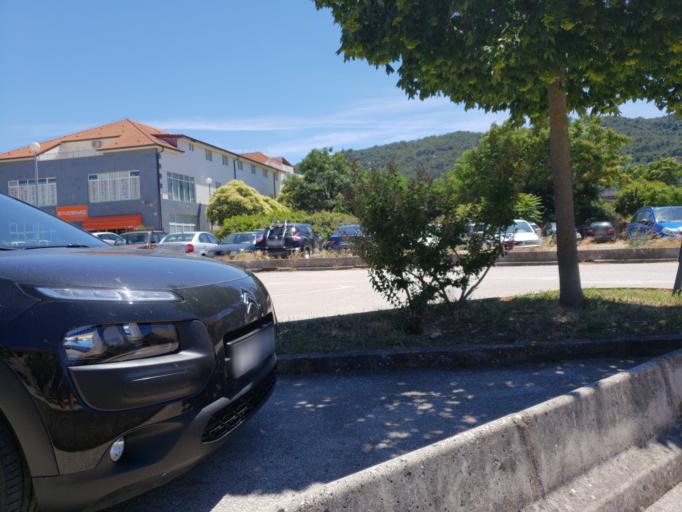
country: HR
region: Splitsko-Dalmatinska
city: Stari Grad
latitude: 43.1837
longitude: 16.6011
